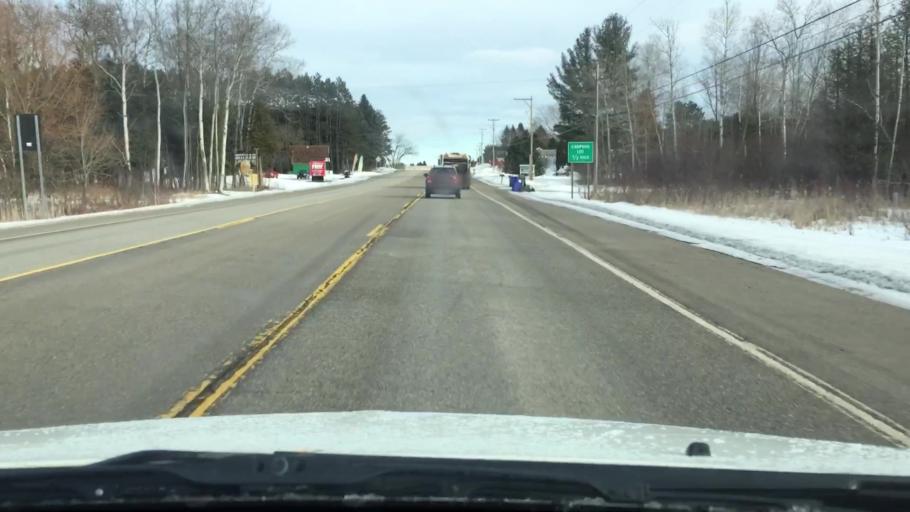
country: US
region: Michigan
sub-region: Wexford County
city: Manton
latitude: 44.4037
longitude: -85.3915
